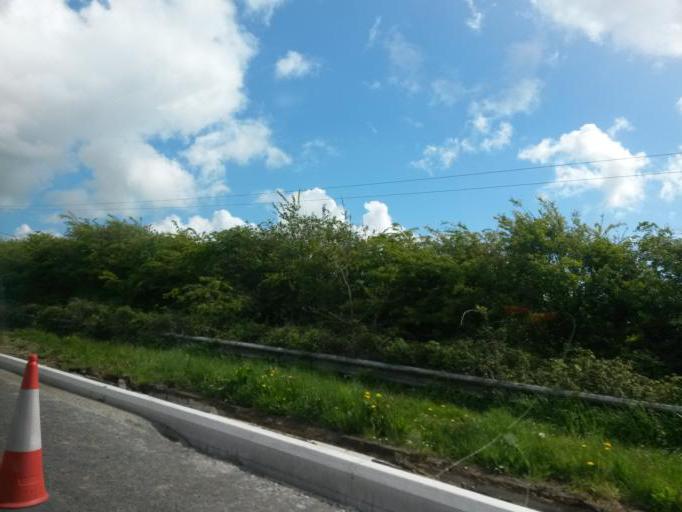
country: IE
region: Leinster
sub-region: Loch Garman
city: Castlebridge
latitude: 52.3828
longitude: -6.5186
